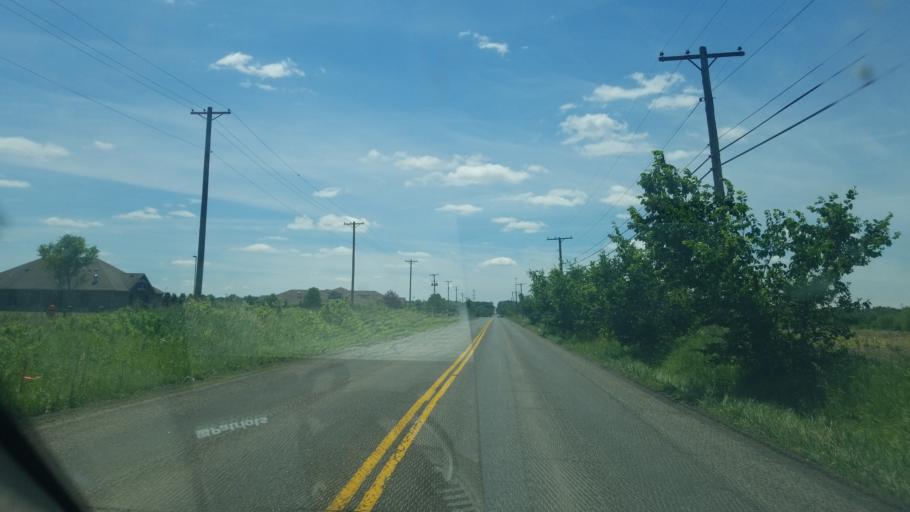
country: US
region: Ohio
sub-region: Columbiana County
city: Columbiana
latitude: 40.8907
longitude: -80.6509
